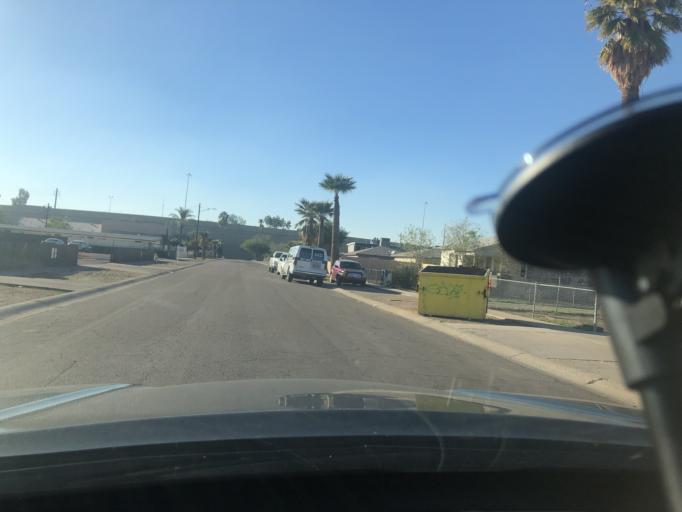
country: US
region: Arizona
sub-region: Maricopa County
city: Phoenix
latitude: 33.4540
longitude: -112.0336
